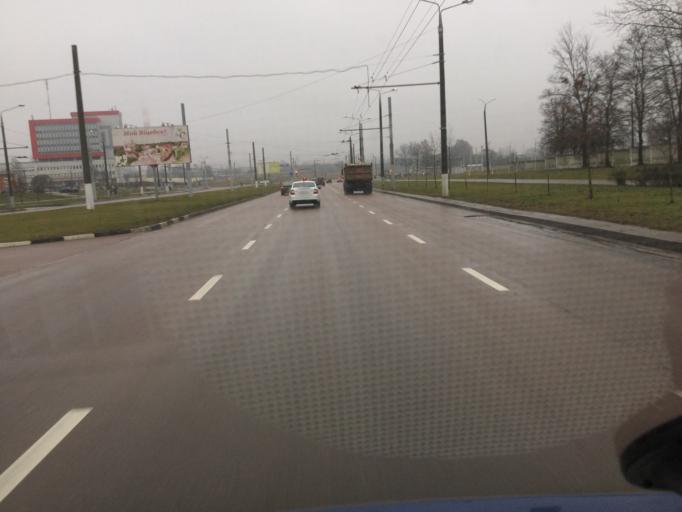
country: BY
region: Vitebsk
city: Vitebsk
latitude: 55.1590
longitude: 30.2301
